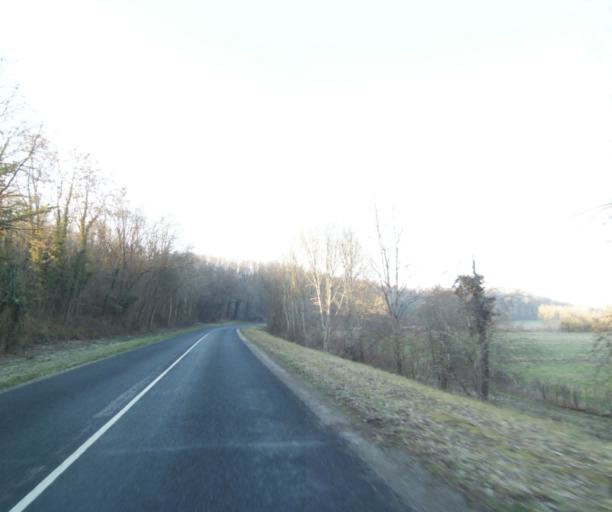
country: FR
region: Champagne-Ardenne
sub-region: Departement de la Haute-Marne
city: Bienville
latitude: 48.5690
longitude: 5.0393
